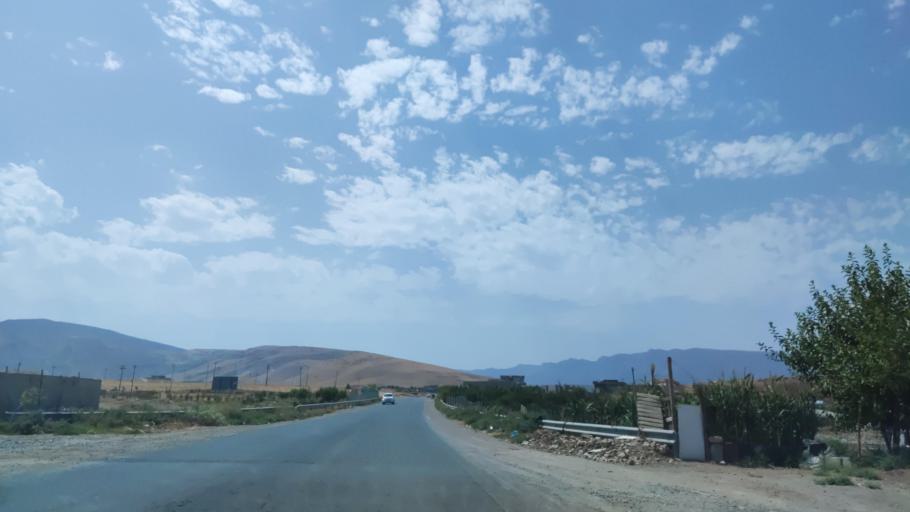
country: IQ
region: Arbil
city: Shaqlawah
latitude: 36.4853
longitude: 44.3975
